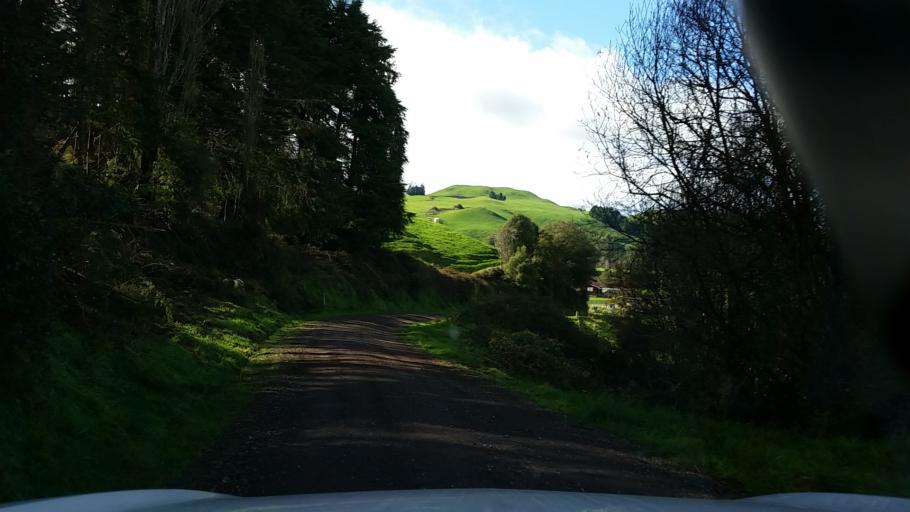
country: NZ
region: Bay of Plenty
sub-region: Rotorua District
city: Rotorua
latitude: -38.4448
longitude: 176.2862
